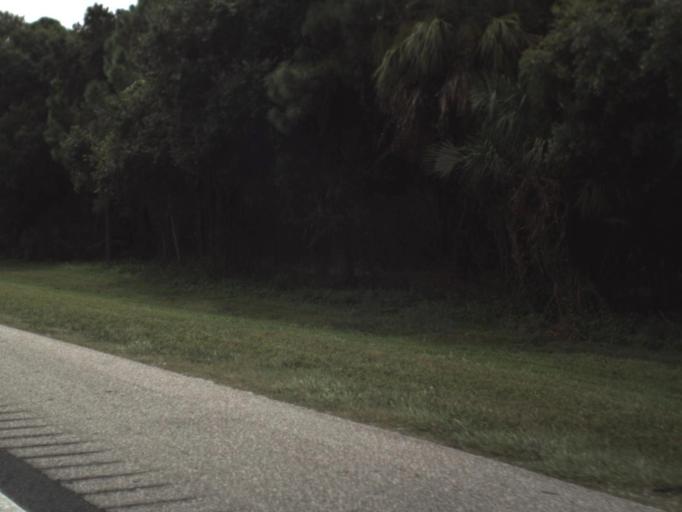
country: US
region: Florida
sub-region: Manatee County
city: Ellenton
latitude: 27.4800
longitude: -82.4671
